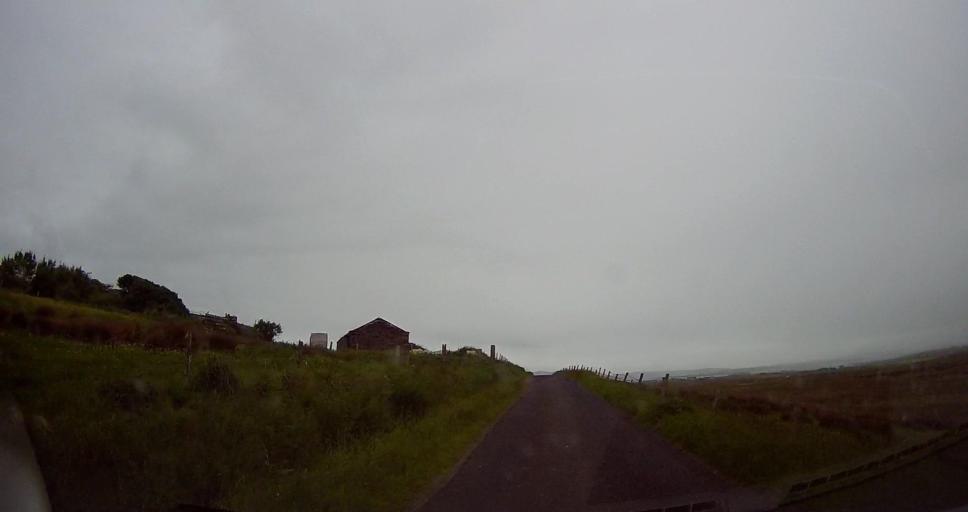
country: GB
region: Scotland
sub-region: Orkney Islands
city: Stromness
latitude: 58.9774
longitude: -3.1667
